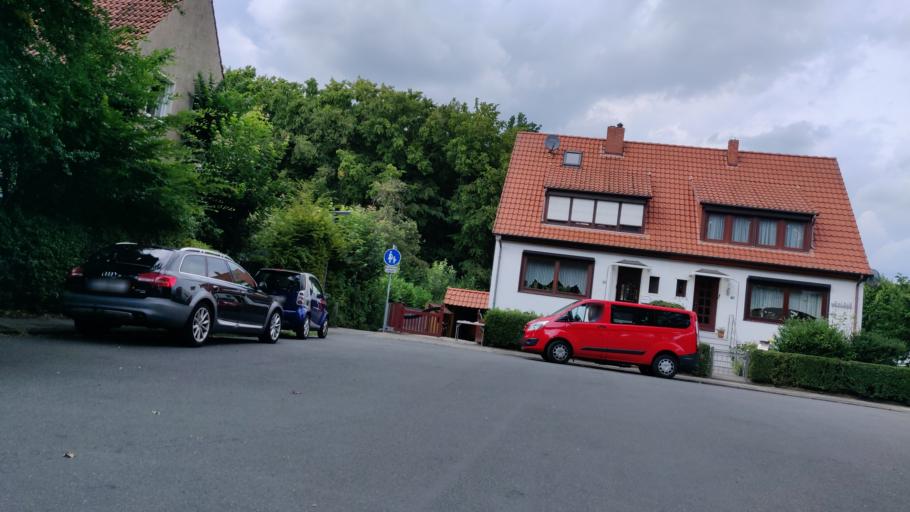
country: DE
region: Lower Saxony
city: Lilienthal
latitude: 53.0959
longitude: 8.8753
